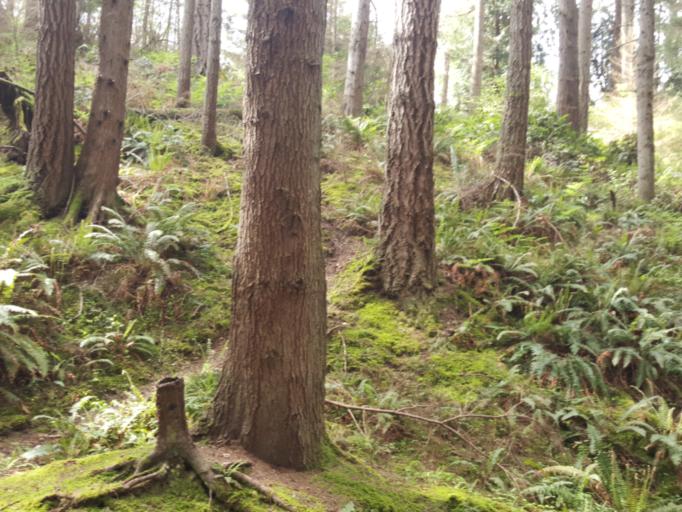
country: US
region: Washington
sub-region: Pierce County
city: University Place
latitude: 47.2051
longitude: -122.5408
